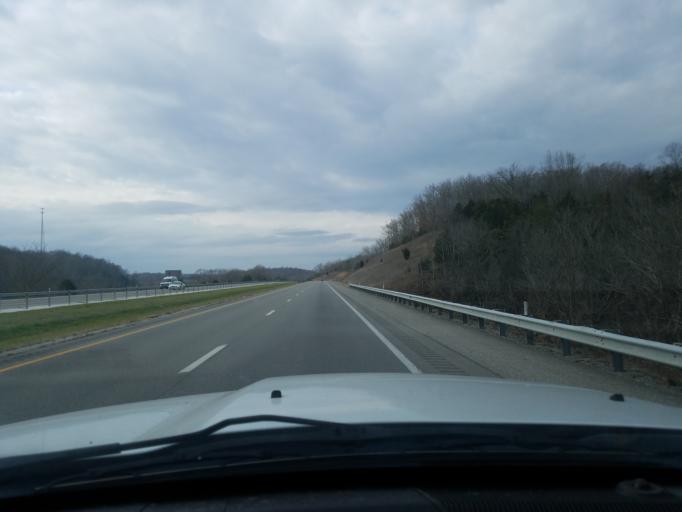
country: US
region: Kentucky
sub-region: Carter County
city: Olive Hill
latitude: 38.3302
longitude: -83.1903
